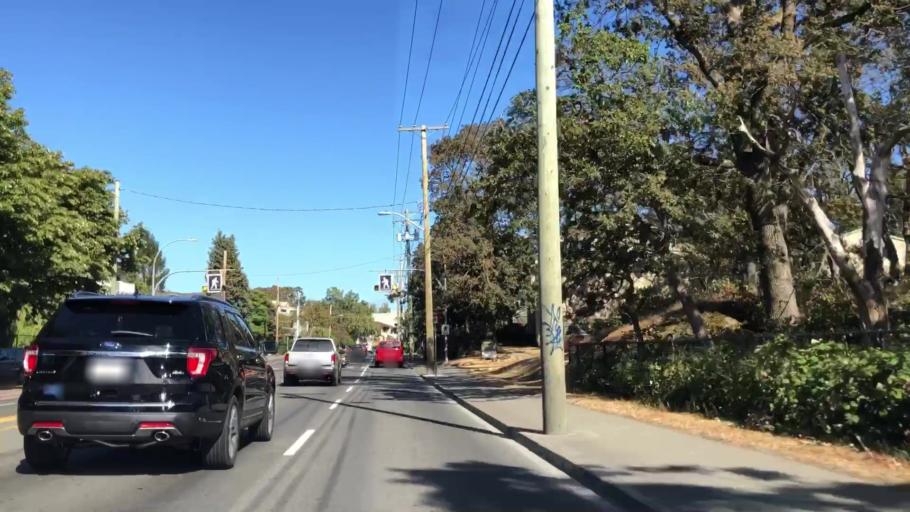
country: CA
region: British Columbia
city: Victoria
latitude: 48.4407
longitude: -123.3499
